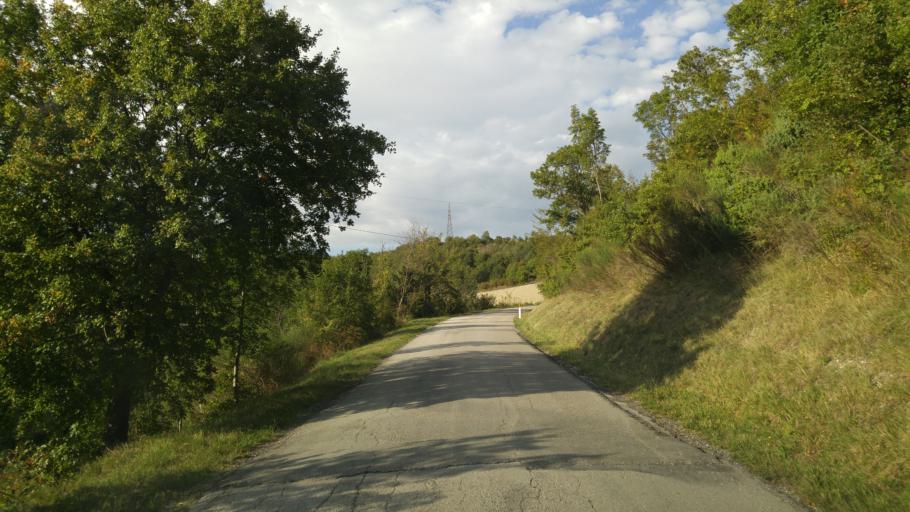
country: IT
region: The Marches
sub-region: Provincia di Pesaro e Urbino
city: Cagli
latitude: 43.5576
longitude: 12.6301
